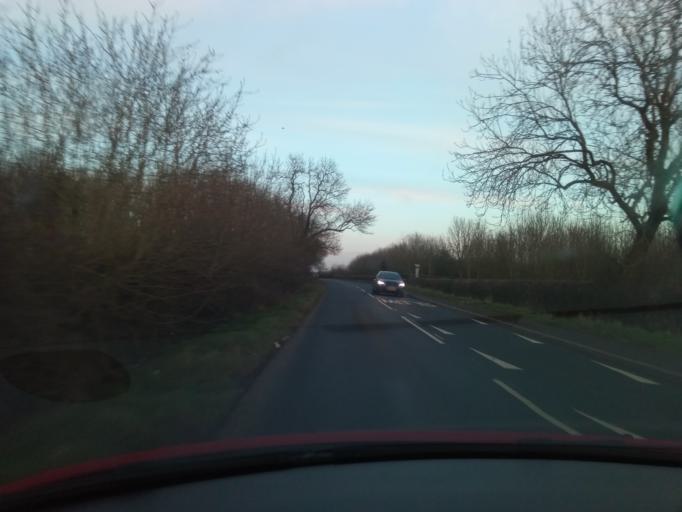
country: GB
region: England
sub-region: Leicestershire
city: Sileby
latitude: 52.7443
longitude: -1.0975
